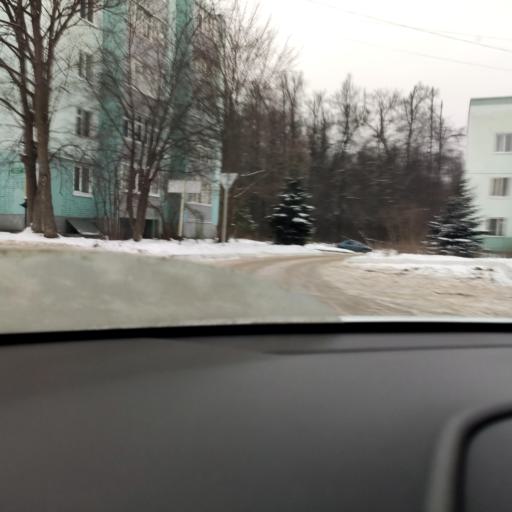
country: RU
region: Tatarstan
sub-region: Zelenodol'skiy Rayon
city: Zelenodolsk
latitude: 55.8553
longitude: 48.4877
